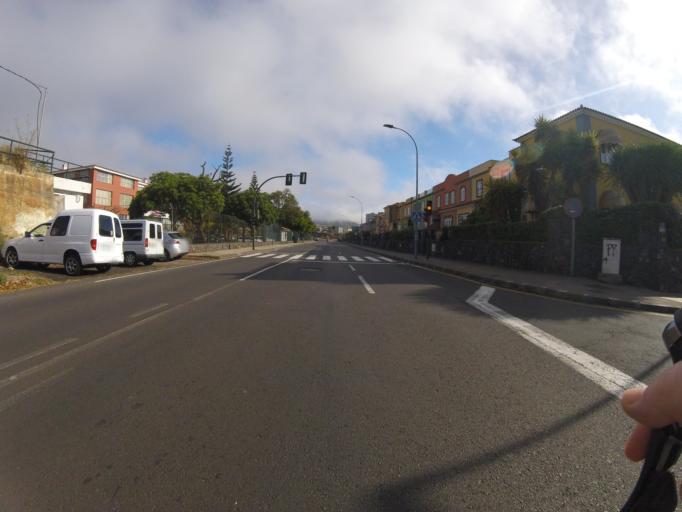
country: ES
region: Canary Islands
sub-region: Provincia de Santa Cruz de Tenerife
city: La Laguna
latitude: 28.4783
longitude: -16.3181
